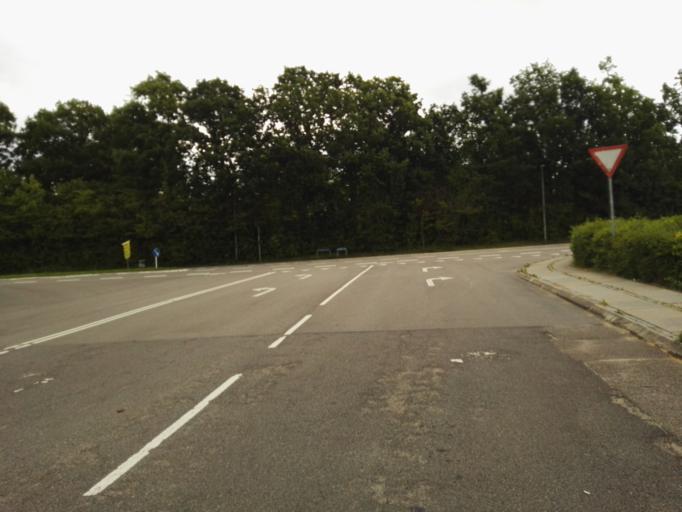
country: DK
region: Capital Region
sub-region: Egedal Kommune
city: Stenlose
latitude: 55.7658
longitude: 12.1960
